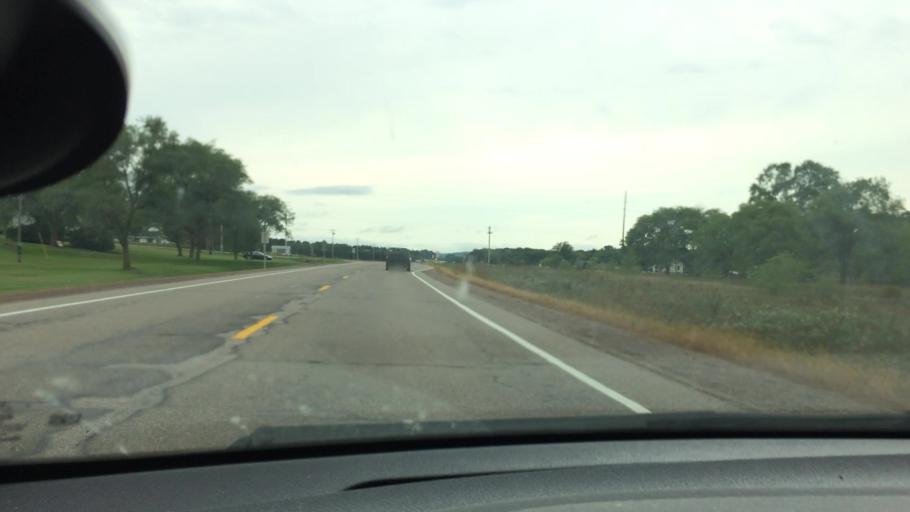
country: US
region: Wisconsin
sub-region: Trempealeau County
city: Osseo
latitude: 44.5864
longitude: -91.1426
